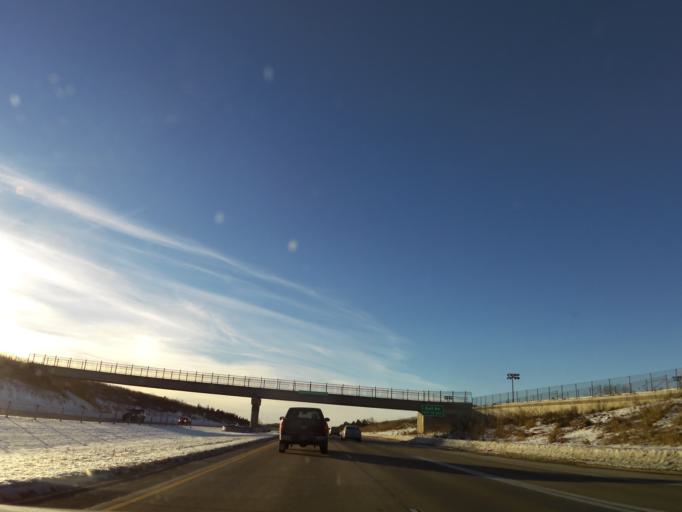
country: US
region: Minnesota
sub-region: Hennepin County
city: Eden Prairie
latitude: 44.8501
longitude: -93.4924
